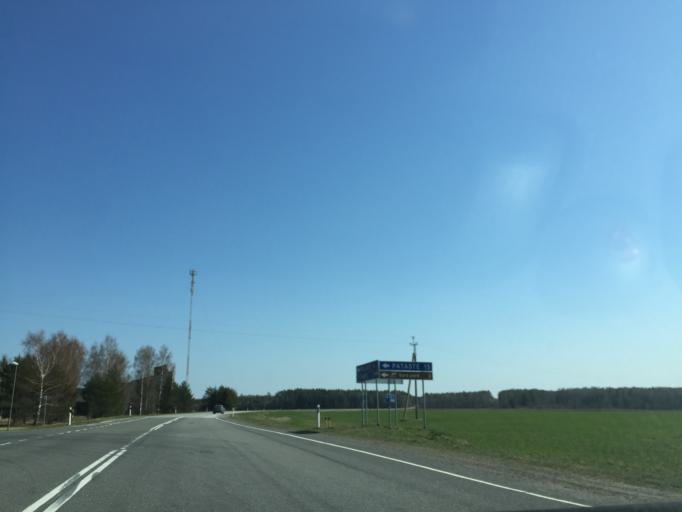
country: EE
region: Tartu
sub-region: Tartu linn
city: Tartu
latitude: 58.5091
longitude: 26.8903
